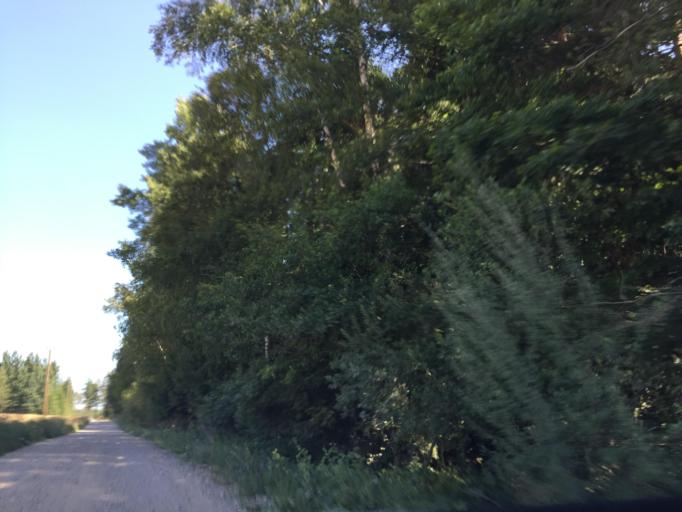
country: LV
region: Talsu Rajons
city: Stende
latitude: 57.1790
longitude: 22.3136
